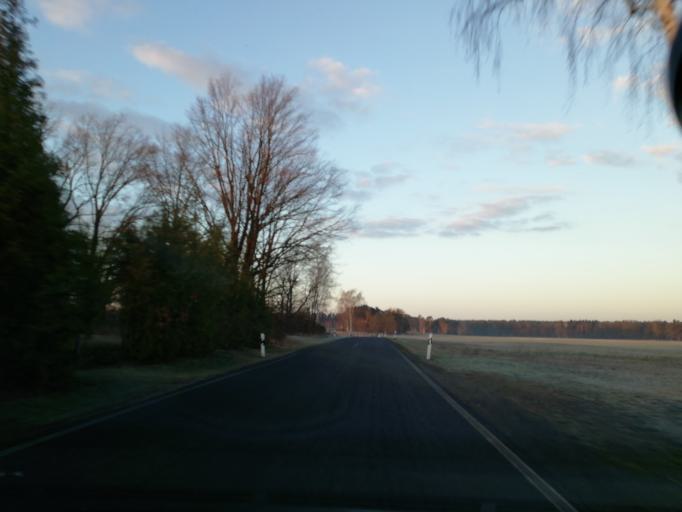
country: DE
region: Brandenburg
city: Calau
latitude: 51.7302
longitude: 13.9048
